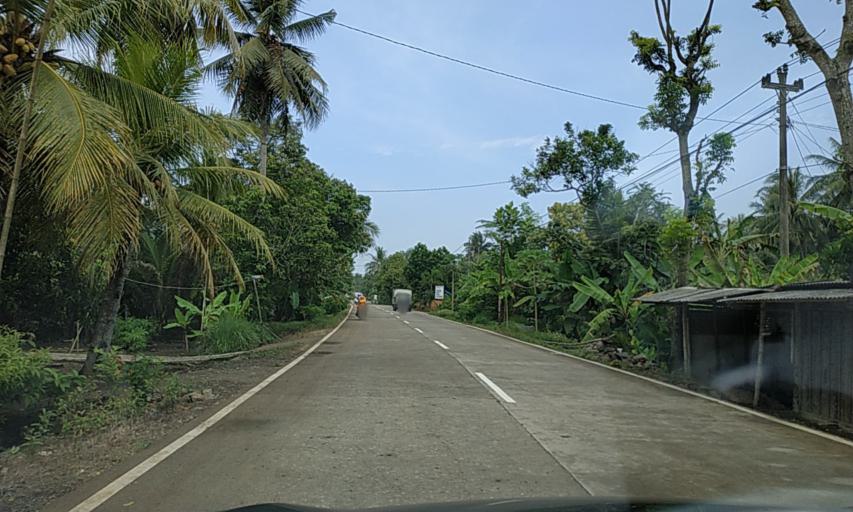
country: ID
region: Central Java
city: Ciloning
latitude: -7.4813
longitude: 108.8377
